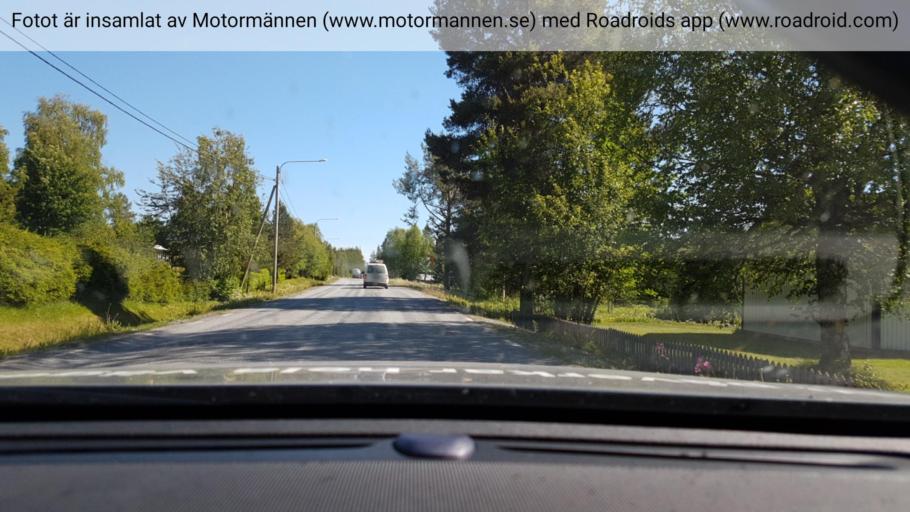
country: SE
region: Vaesterbotten
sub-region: Vilhelmina Kommun
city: Sjoberg
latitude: 64.6917
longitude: 16.2685
